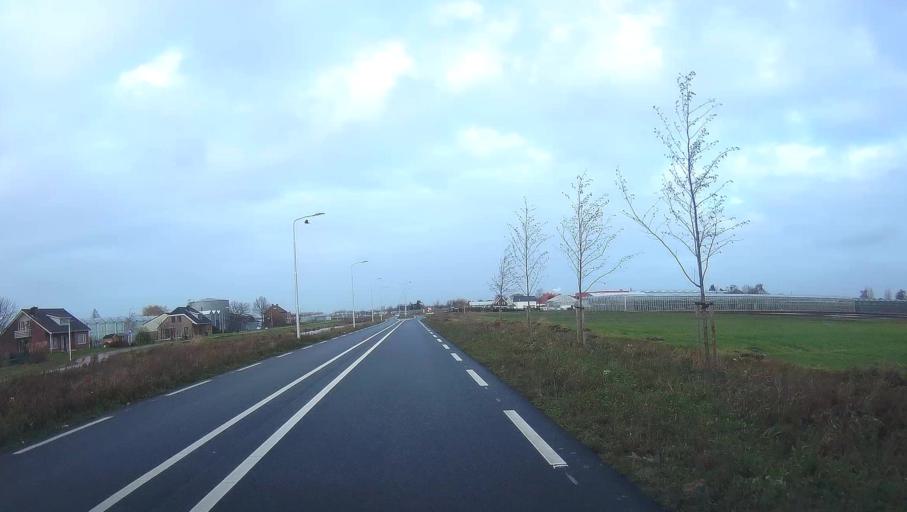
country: NL
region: South Holland
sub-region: Gemeente Pijnacker-Nootdorp
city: Pijnacker
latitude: 52.0101
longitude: 4.4161
